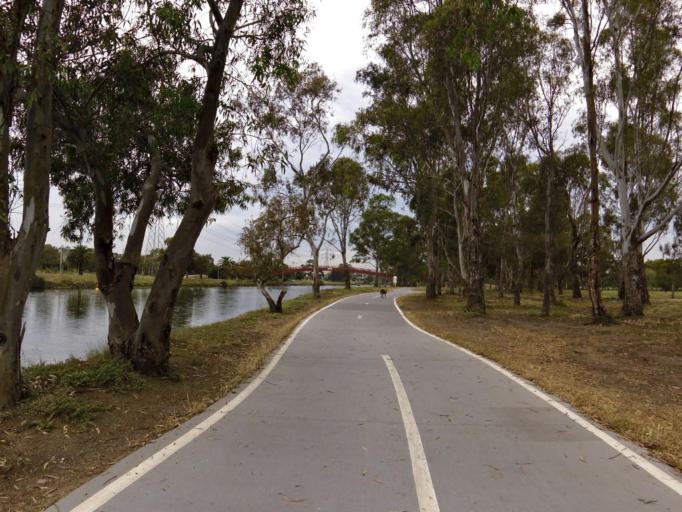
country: AU
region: Victoria
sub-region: Maribyrnong
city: Maribyrnong
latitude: -37.7758
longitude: 144.8960
